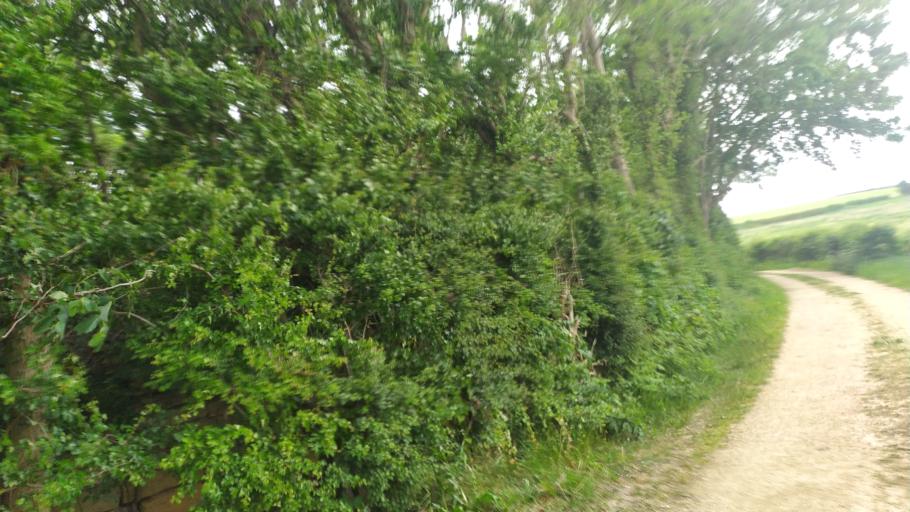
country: GB
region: England
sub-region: City and Borough of Leeds
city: Thorner
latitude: 53.8643
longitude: -1.3972
